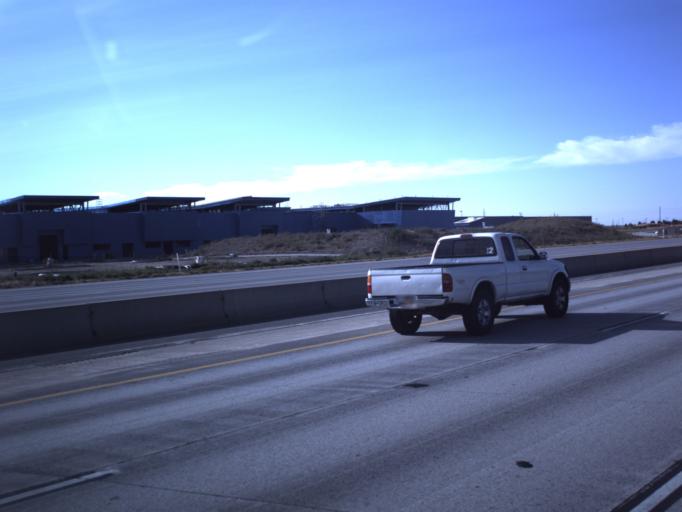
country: US
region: Utah
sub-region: Salt Lake County
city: Salt Lake City
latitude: 40.7918
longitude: -111.9491
